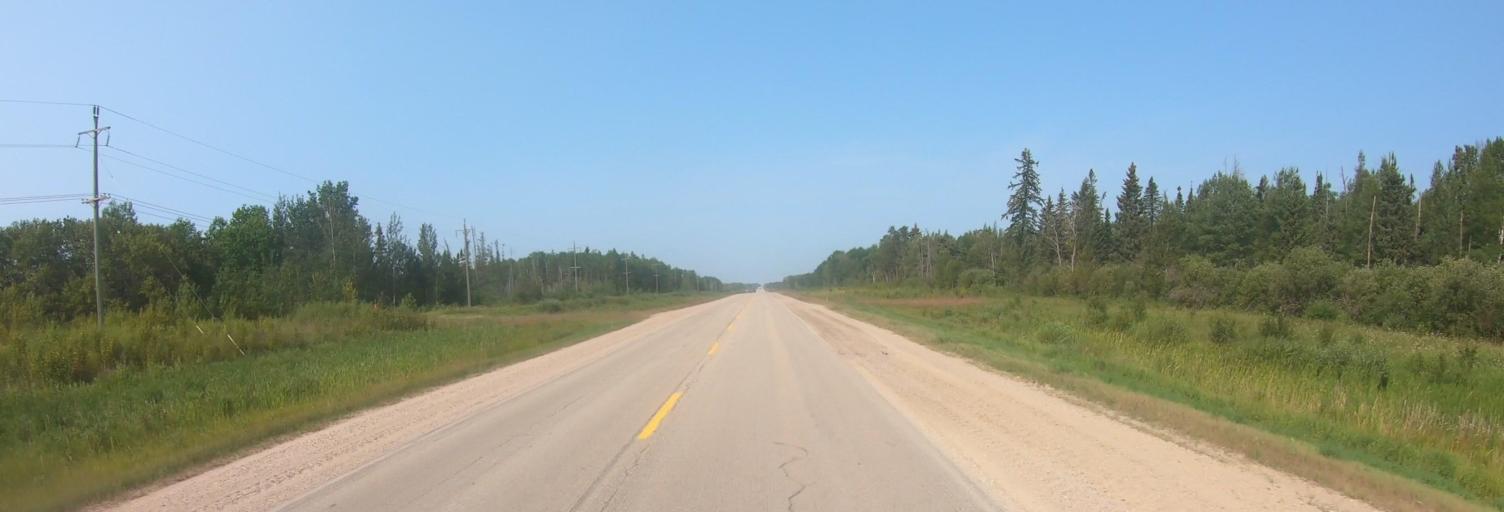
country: US
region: Minnesota
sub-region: Roseau County
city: Roseau
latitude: 49.0896
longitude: -95.9221
